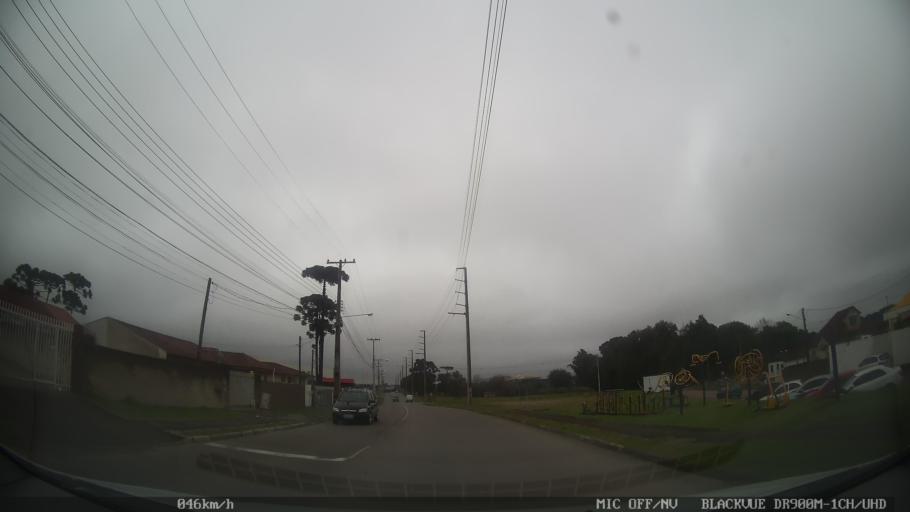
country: BR
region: Parana
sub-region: Sao Jose Dos Pinhais
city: Sao Jose dos Pinhais
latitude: -25.5822
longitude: -49.1704
